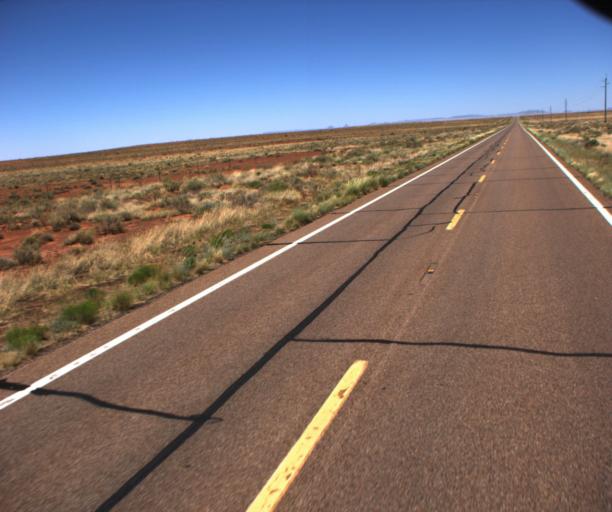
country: US
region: Arizona
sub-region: Coconino County
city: LeChee
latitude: 34.9324
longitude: -110.7945
